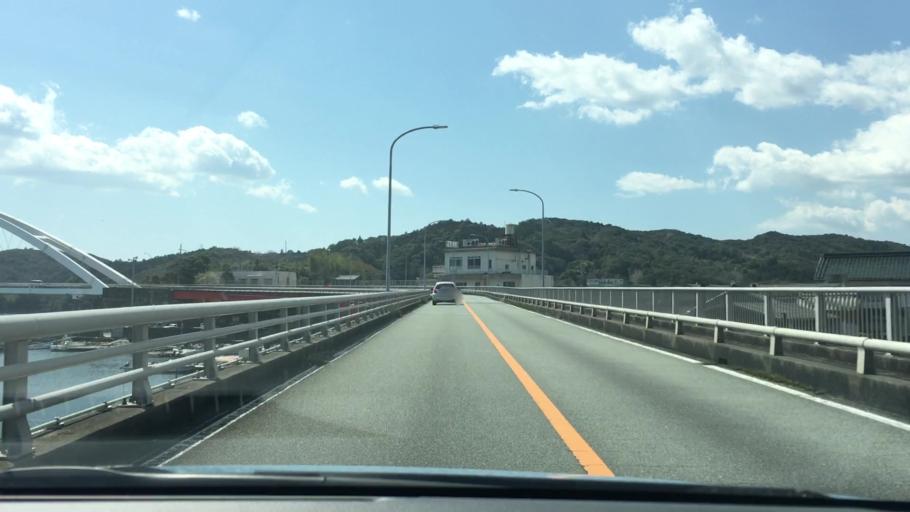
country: JP
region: Mie
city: Toba
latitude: 34.4428
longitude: 136.8805
